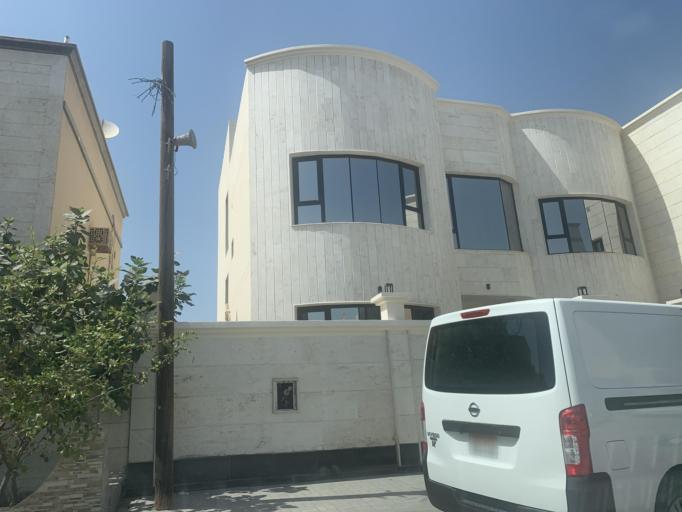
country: BH
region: Manama
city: Jidd Hafs
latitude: 26.2352
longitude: 50.5101
